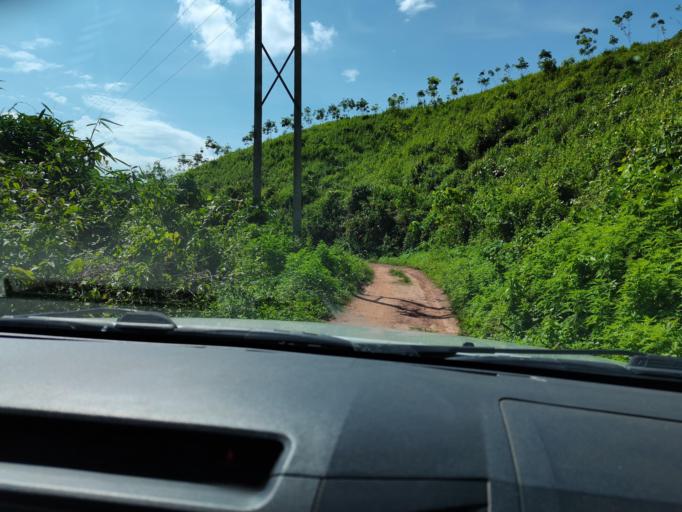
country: LA
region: Loungnamtha
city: Muang Nale
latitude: 20.5553
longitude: 101.0650
